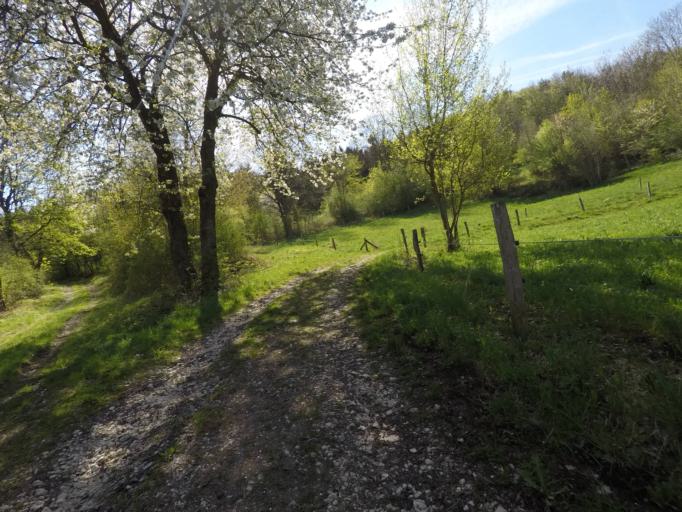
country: DE
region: Baden-Wuerttemberg
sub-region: Tuebingen Region
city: Pfullingen
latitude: 48.4474
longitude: 9.2332
